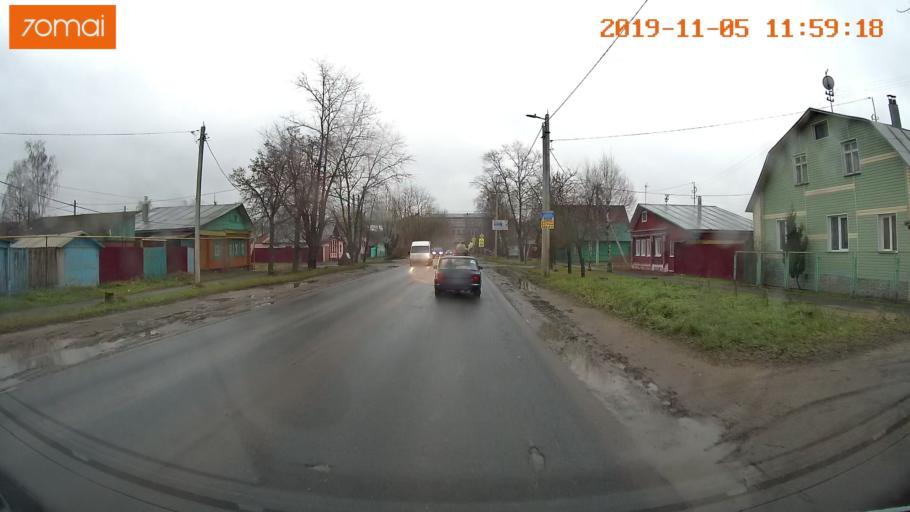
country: RU
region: Ivanovo
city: Kokhma
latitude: 56.9787
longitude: 41.0470
